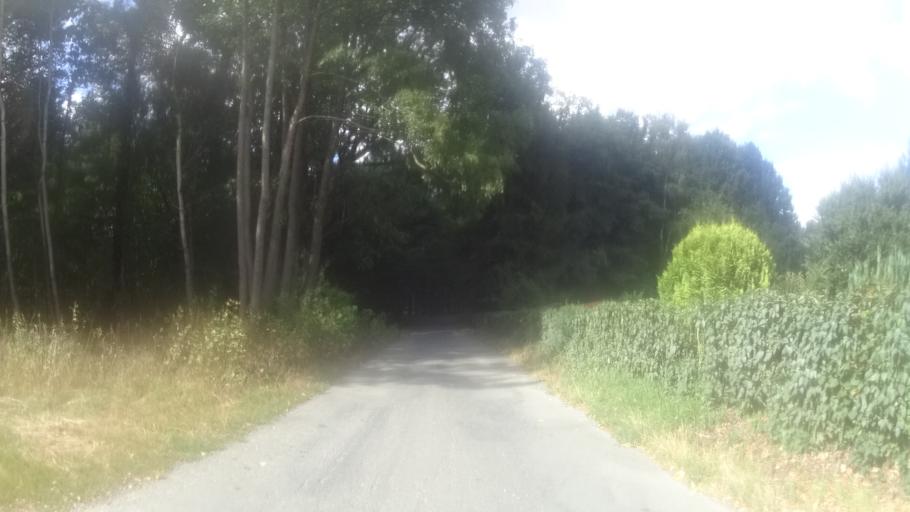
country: CZ
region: Pardubicky
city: Horni Jeleni
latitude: 50.0476
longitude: 16.1567
